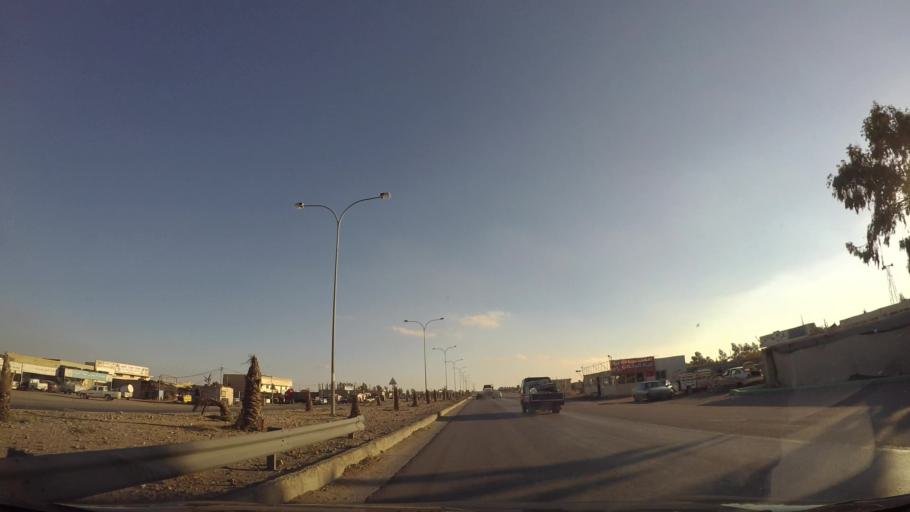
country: JO
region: Tafielah
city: Busayra
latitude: 30.5950
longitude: 35.8036
